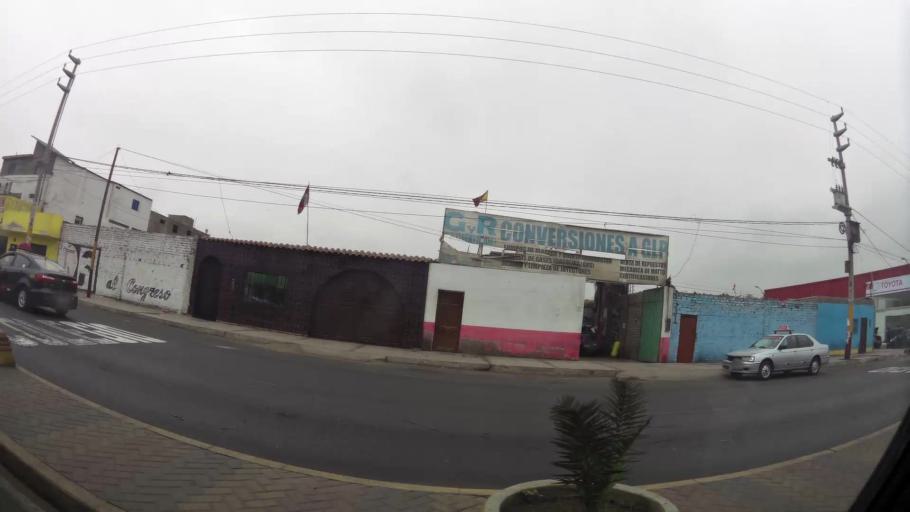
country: PE
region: Ancash
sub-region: Provincia de Santa
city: Chimbote
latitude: -9.0799
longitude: -78.5824
